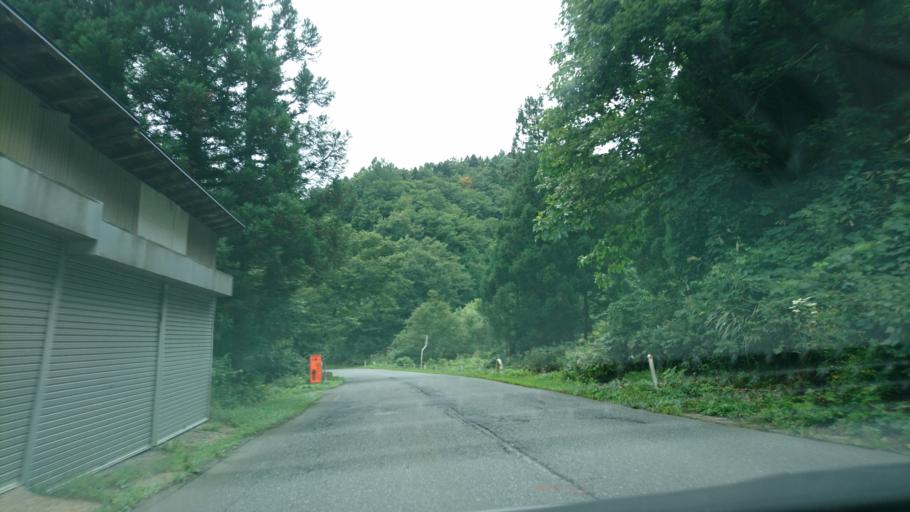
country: JP
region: Yamagata
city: Obanazawa
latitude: 38.8305
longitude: 140.6371
